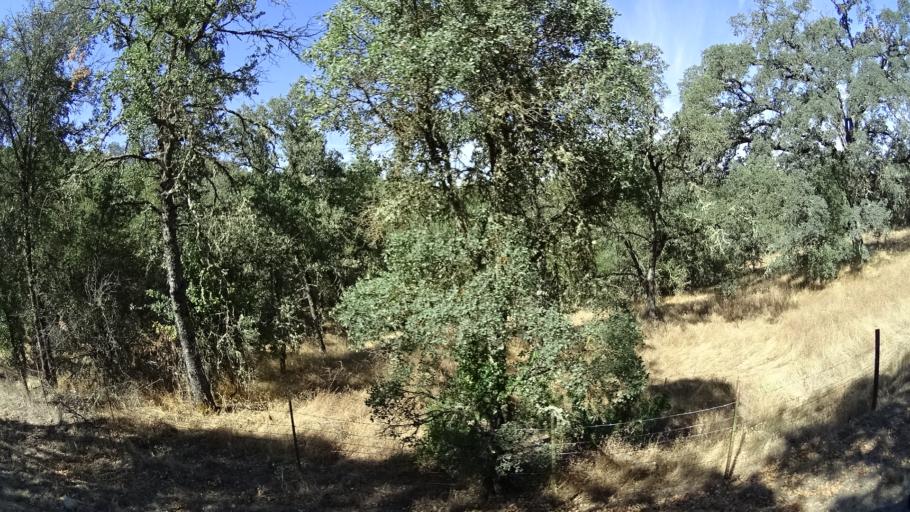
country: US
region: California
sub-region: Calaveras County
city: San Andreas
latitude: 38.1517
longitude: -120.6137
